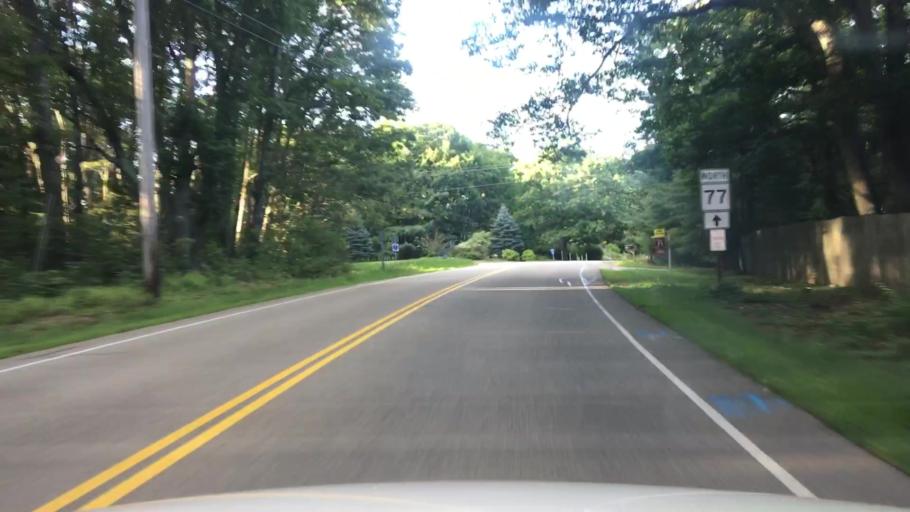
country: US
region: Maine
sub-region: Cumberland County
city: Scarborough
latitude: 43.5717
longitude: -70.2805
